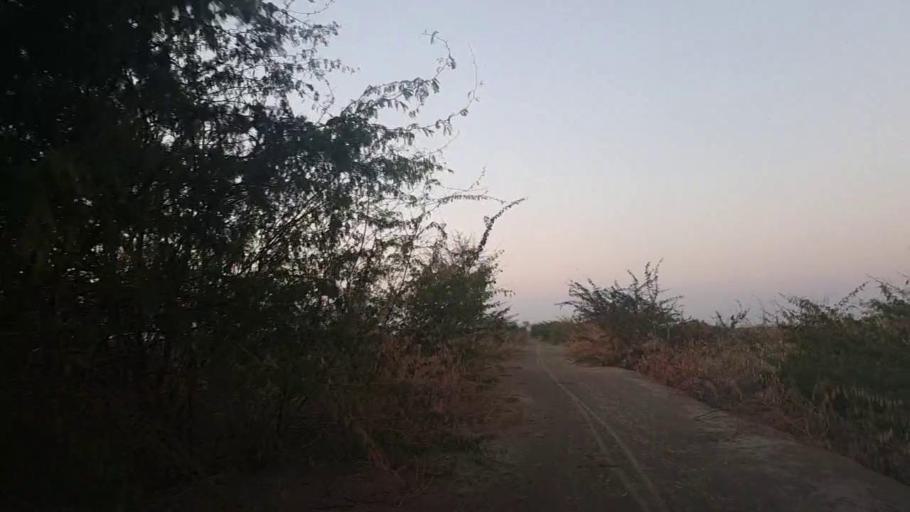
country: PK
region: Sindh
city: Tando Mittha Khan
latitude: 26.0821
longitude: 69.1514
